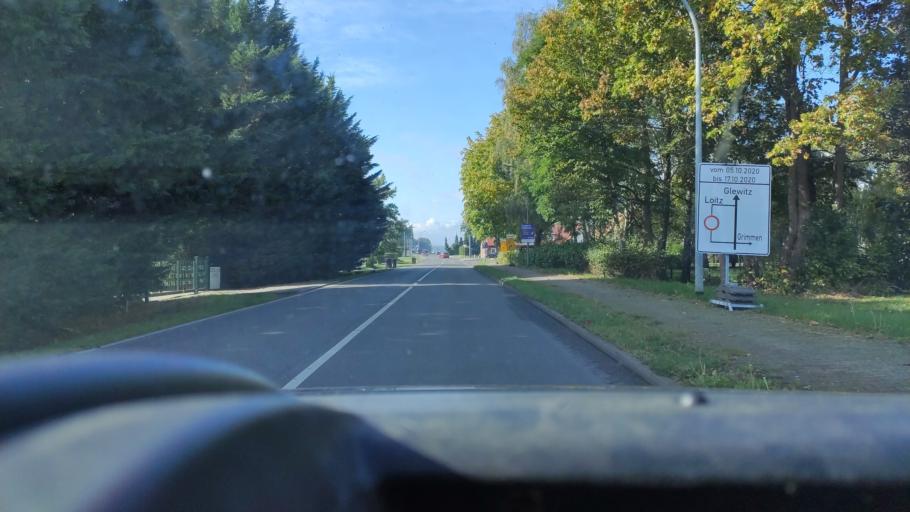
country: DE
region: Mecklenburg-Vorpommern
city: Grimmen
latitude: 54.0540
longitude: 13.1211
